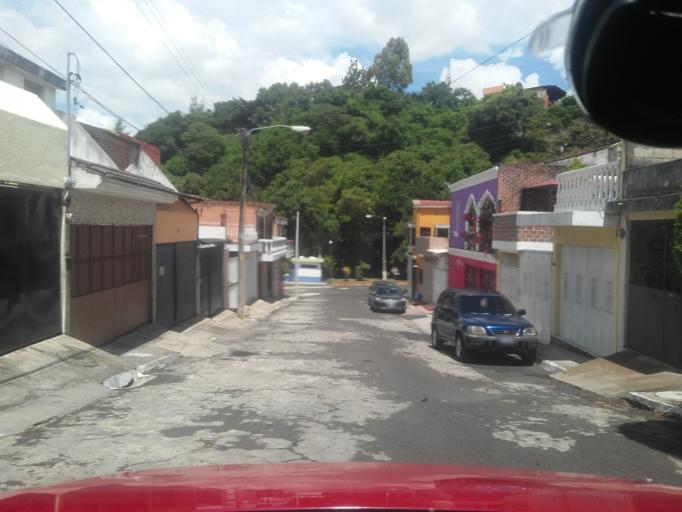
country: GT
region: Guatemala
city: Mixco
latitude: 14.6464
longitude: -90.5650
